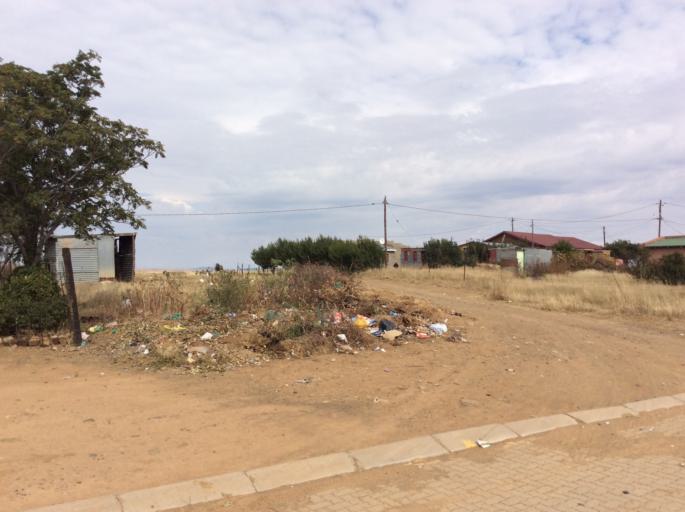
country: LS
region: Mafeteng
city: Mafeteng
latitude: -29.7216
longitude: 27.0082
